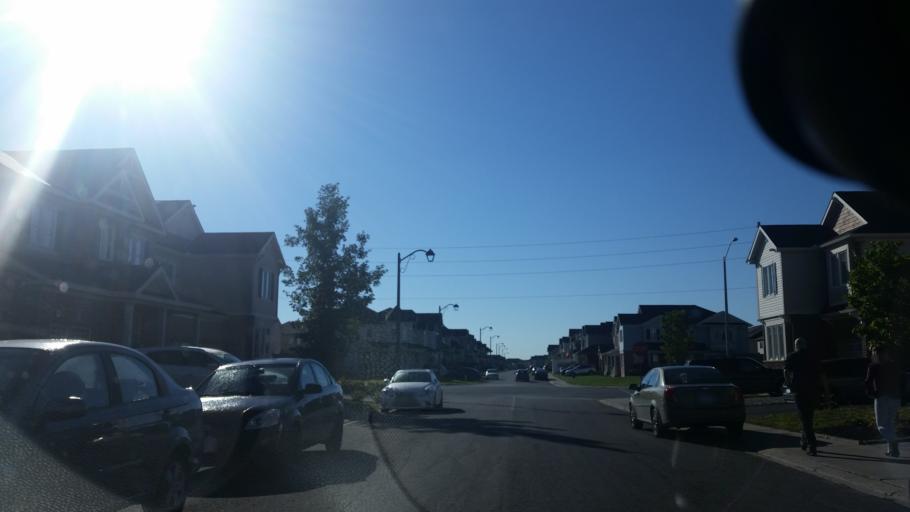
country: CA
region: Ontario
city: Bells Corners
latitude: 45.2506
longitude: -75.7439
